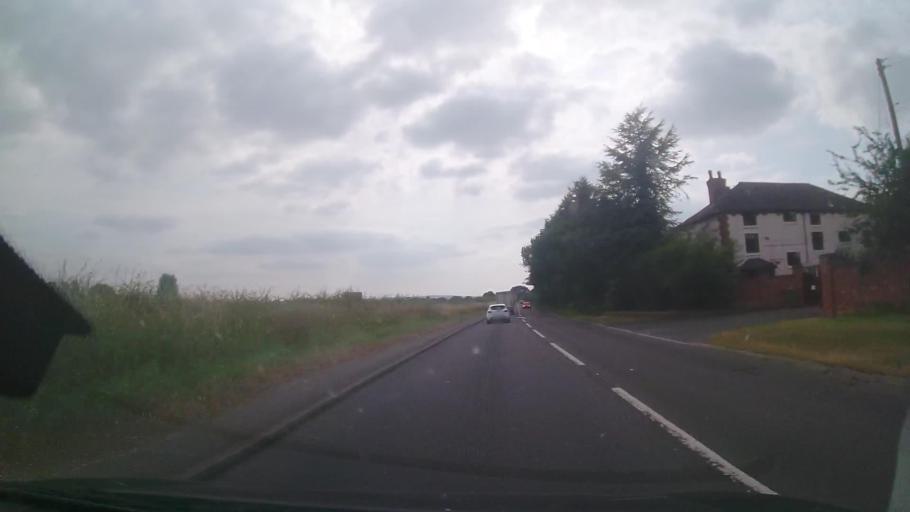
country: GB
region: England
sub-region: Shropshire
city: Market Drayton
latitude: 52.8935
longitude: -2.5267
